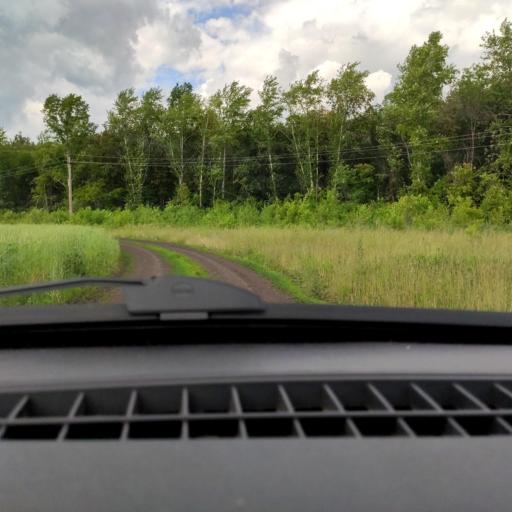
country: RU
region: Bashkortostan
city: Kabakovo
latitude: 54.5226
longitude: 56.0686
